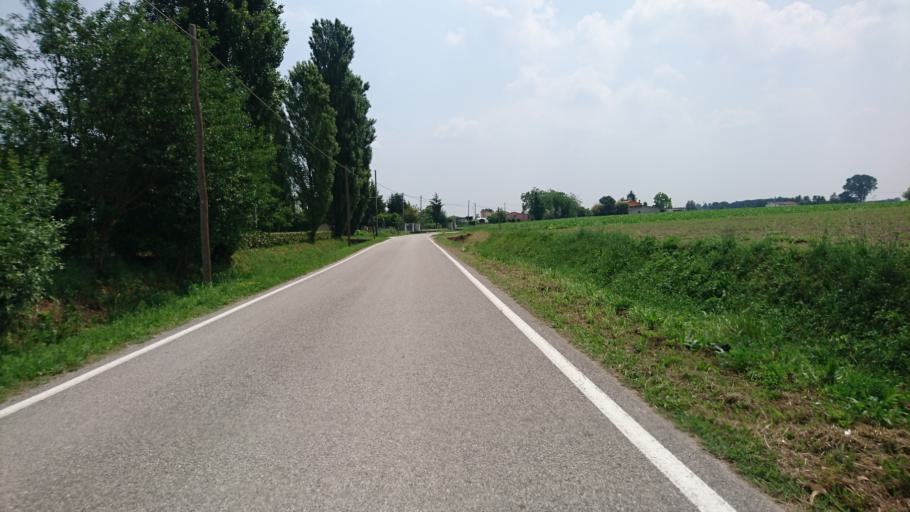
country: IT
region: Veneto
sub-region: Provincia di Padova
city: Cartura
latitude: 45.2622
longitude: 11.8818
